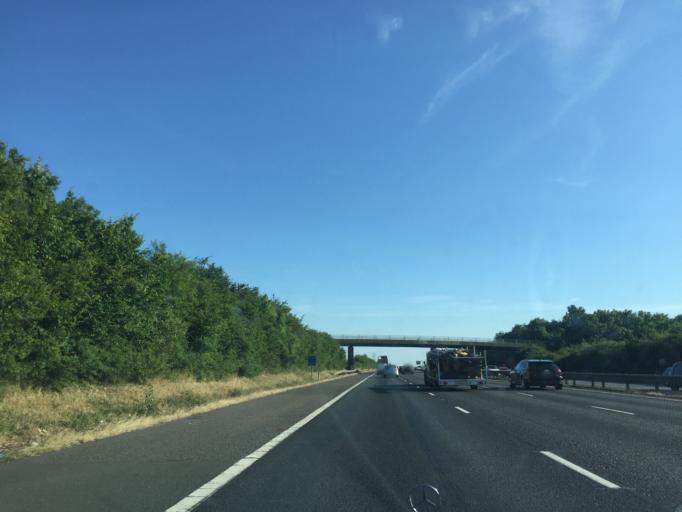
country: GB
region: England
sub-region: Oxfordshire
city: Bicester
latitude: 51.9192
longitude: -1.2029
